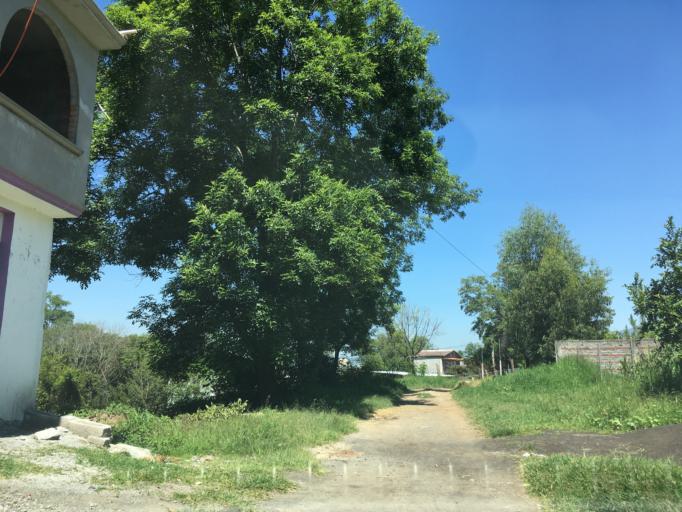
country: MX
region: Michoacan
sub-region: Morelia
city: Morelos
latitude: 19.6488
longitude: -101.2346
